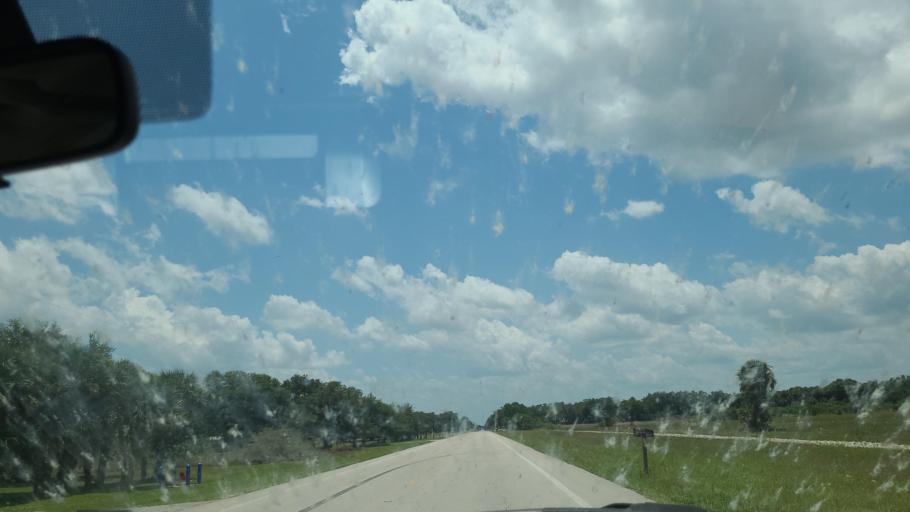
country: US
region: Florida
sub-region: Glades County
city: Buckhead Ridge
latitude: 27.0991
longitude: -81.0700
